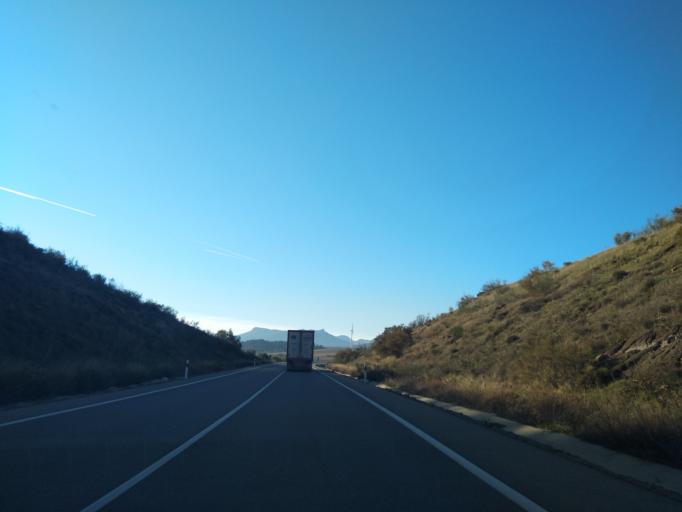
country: ES
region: Andalusia
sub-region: Provincia de Malaga
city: Teba
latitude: 36.9582
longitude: -4.8583
